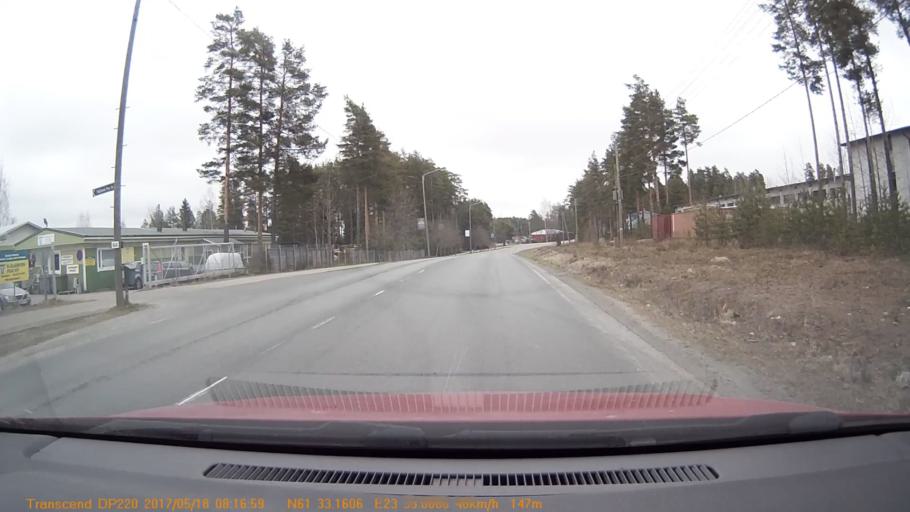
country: FI
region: Pirkanmaa
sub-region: Tampere
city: Yloejaervi
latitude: 61.5527
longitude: 23.5627
